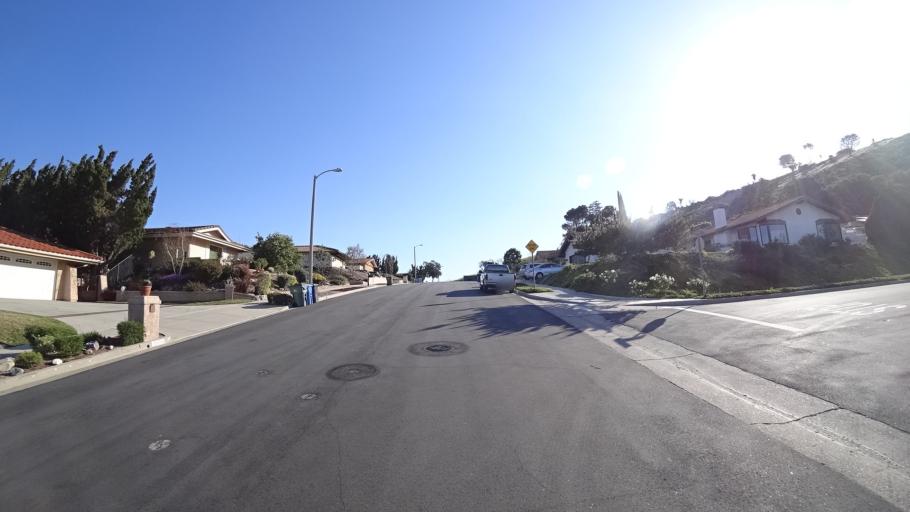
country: US
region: California
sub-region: Ventura County
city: Thousand Oaks
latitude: 34.1974
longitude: -118.8396
